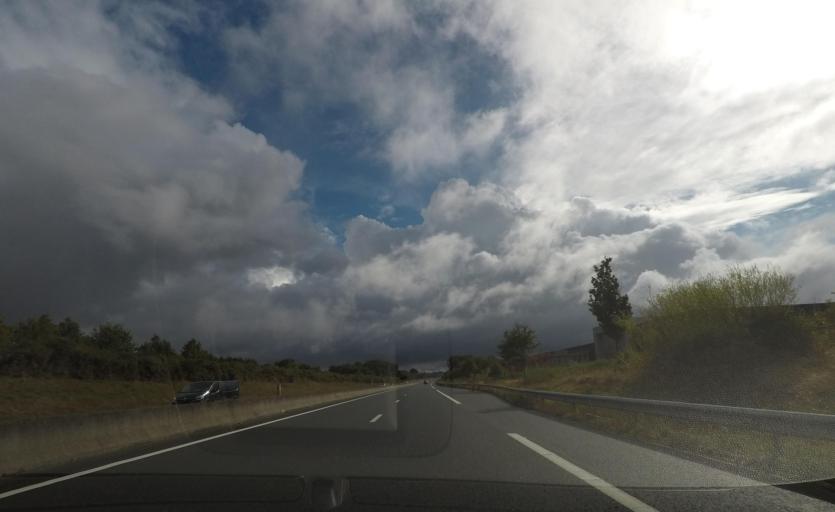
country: FR
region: Pays de la Loire
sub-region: Departement de la Vendee
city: La Roche-sur-Yon
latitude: 46.6656
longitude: -1.3643
